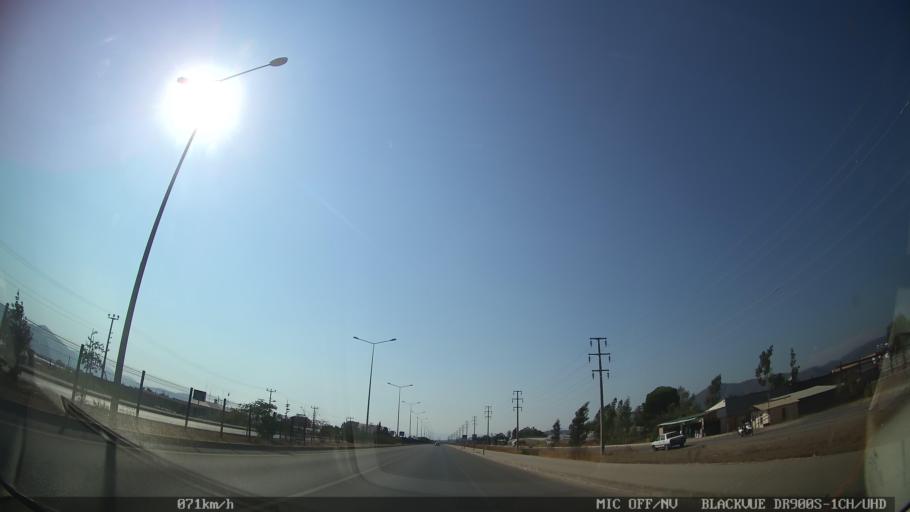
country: TR
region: Mugla
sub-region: Fethiye
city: Fethiye
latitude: 36.6528
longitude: 29.1724
